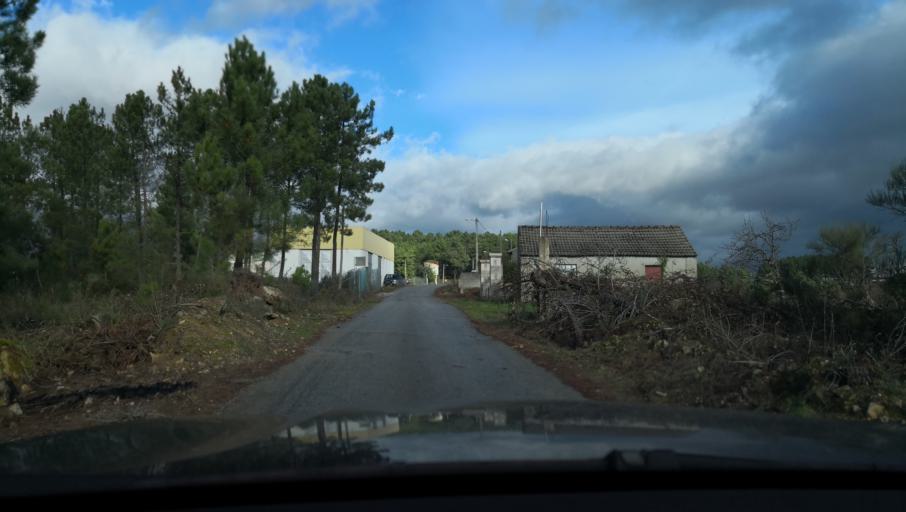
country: PT
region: Vila Real
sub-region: Vila Real
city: Vila Real
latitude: 41.2702
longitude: -7.7155
